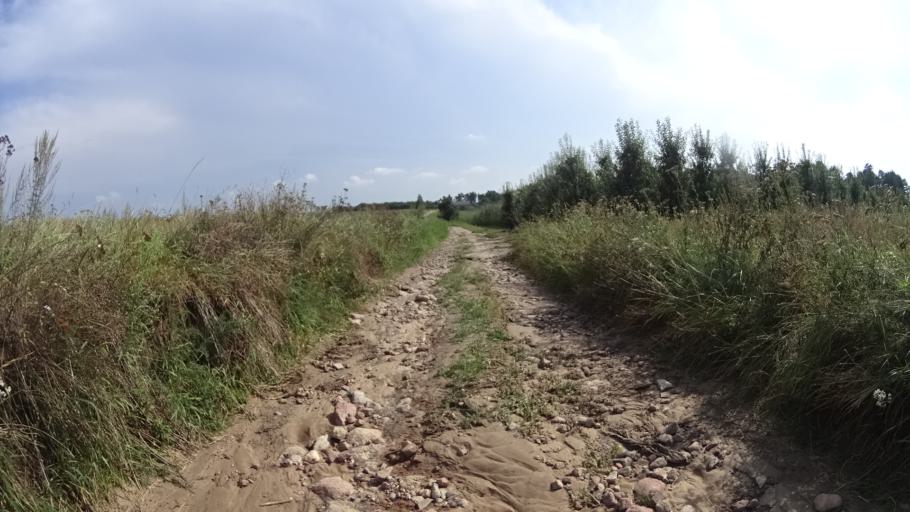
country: PL
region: Masovian Voivodeship
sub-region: Powiat grojecki
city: Goszczyn
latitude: 51.6901
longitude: 20.8392
